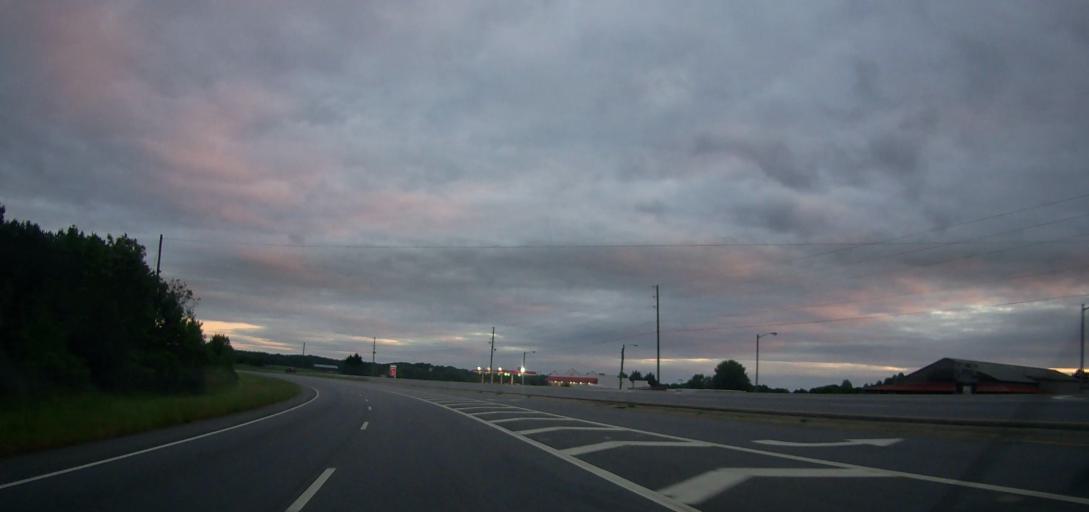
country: US
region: Georgia
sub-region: Jackson County
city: Arcade
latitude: 34.0371
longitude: -83.5002
